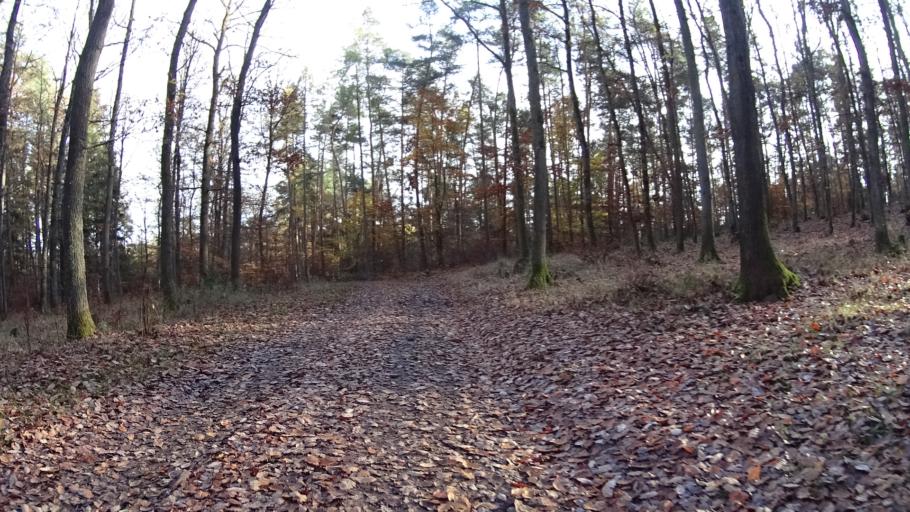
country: DE
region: Rheinland-Pfalz
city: Hoppstadten
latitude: 49.6851
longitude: 7.5221
